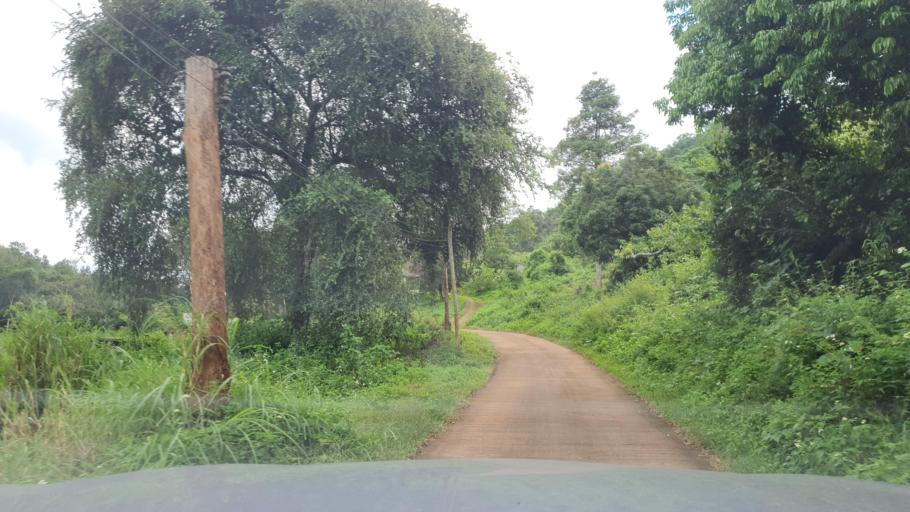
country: TH
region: Chiang Mai
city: Samoeng
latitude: 18.8066
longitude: 98.8195
